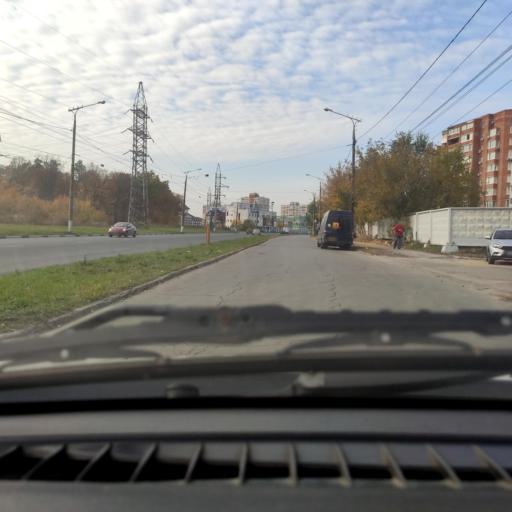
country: RU
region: Samara
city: Tol'yatti
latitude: 53.5029
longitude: 49.4277
